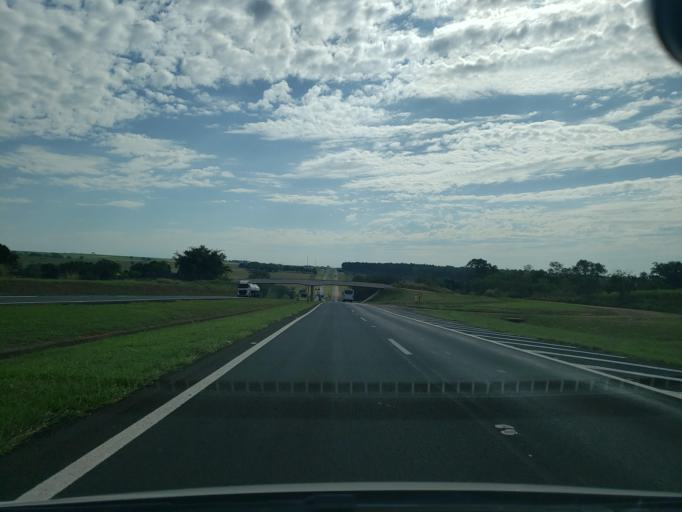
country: BR
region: Sao Paulo
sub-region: Promissao
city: Promissao
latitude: -21.6134
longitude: -49.8653
